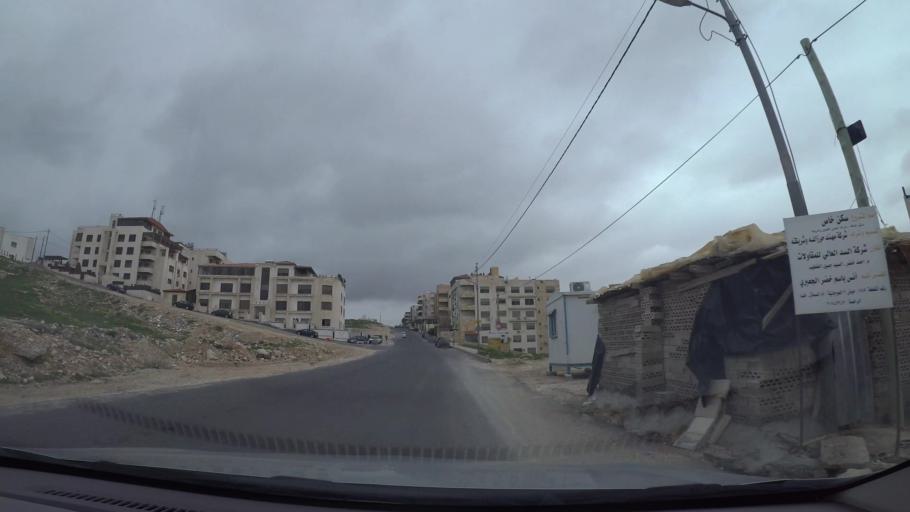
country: JO
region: Amman
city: Wadi as Sir
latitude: 31.9910
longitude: 35.8373
